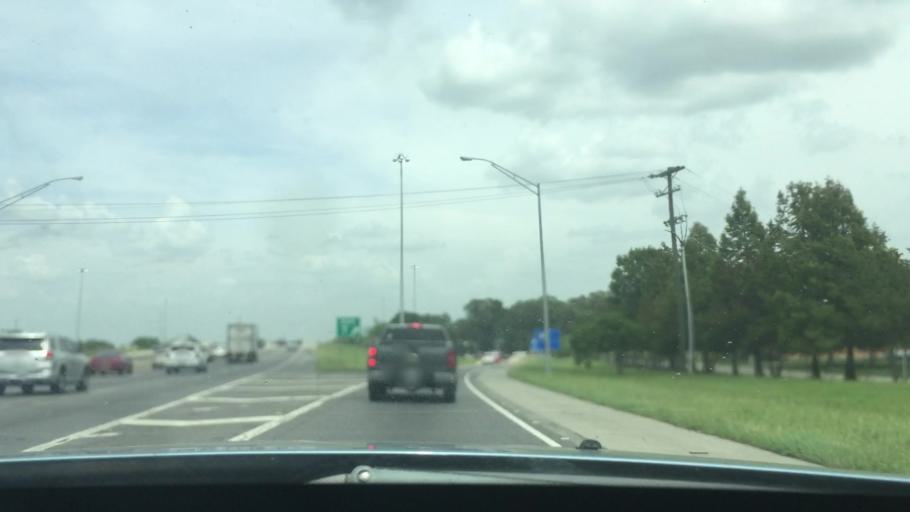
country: US
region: Louisiana
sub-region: East Baton Rouge Parish
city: Shenandoah
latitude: 30.4413
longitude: -91.0113
